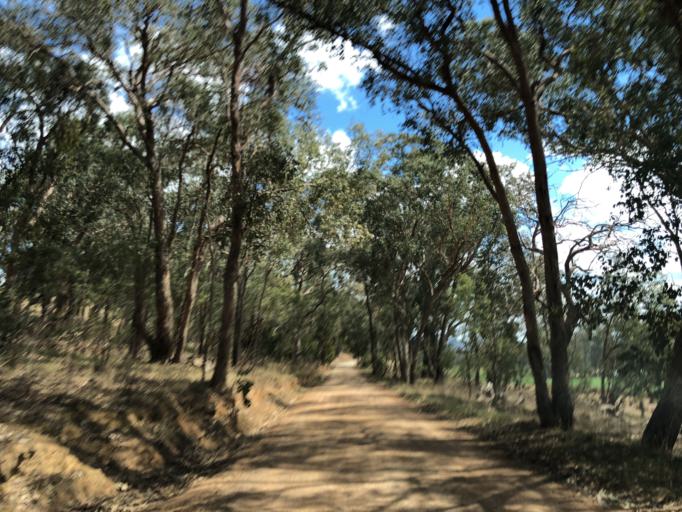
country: AU
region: Victoria
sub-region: Benalla
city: Benalla
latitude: -36.7297
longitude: 146.1255
